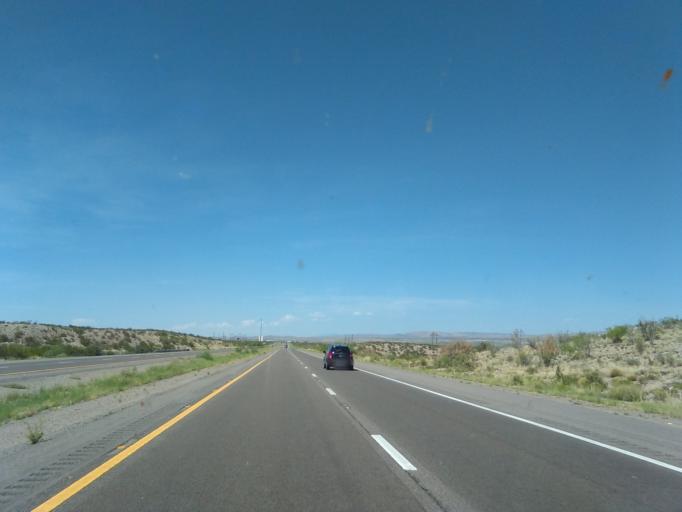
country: US
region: New Mexico
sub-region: Socorro County
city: Socorro
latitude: 33.9002
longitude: -106.8885
